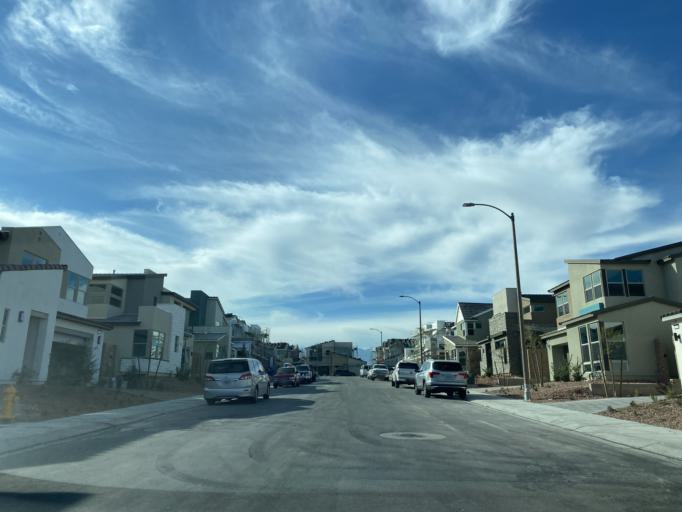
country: US
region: Nevada
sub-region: Clark County
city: Summerlin South
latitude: 36.3126
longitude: -115.3194
